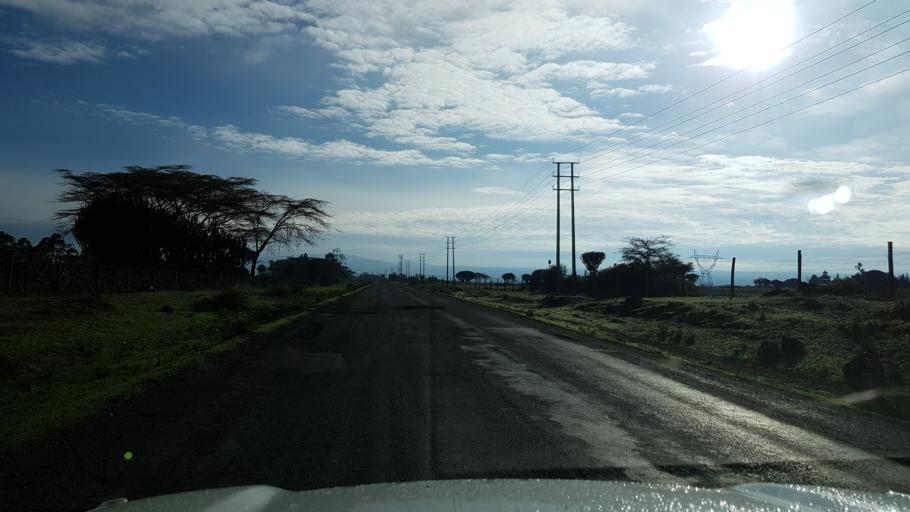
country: KE
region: Nakuru
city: Naivasha
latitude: -0.8190
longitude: 36.3898
